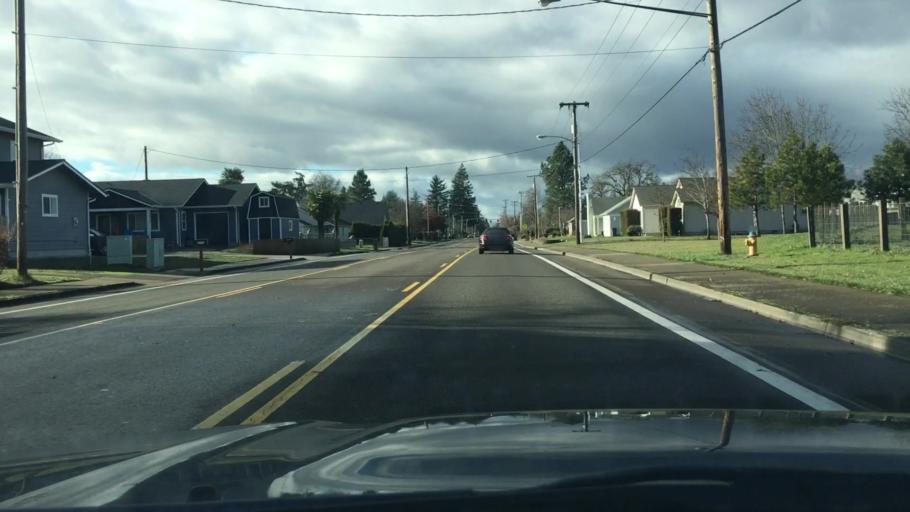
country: US
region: Oregon
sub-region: Lane County
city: Eugene
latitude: 44.0701
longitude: -123.1841
